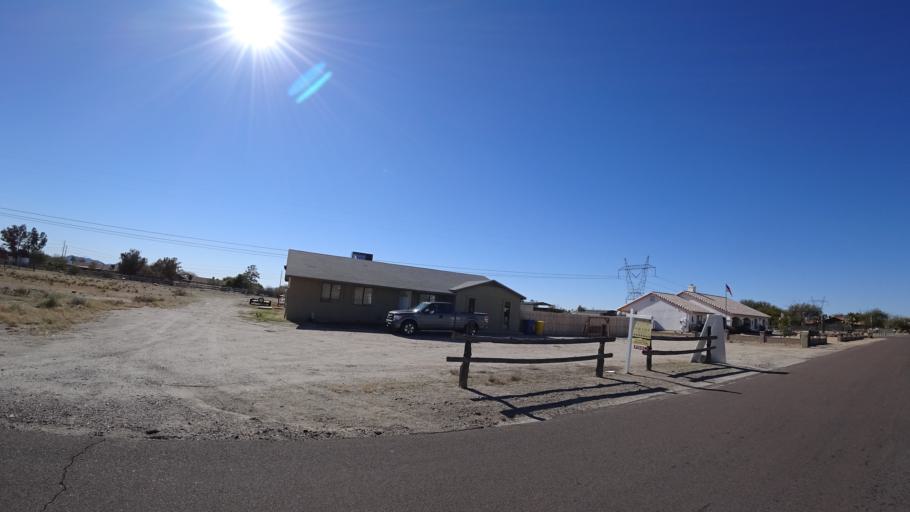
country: US
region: Arizona
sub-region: Maricopa County
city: Buckeye
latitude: 33.4250
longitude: -112.5322
